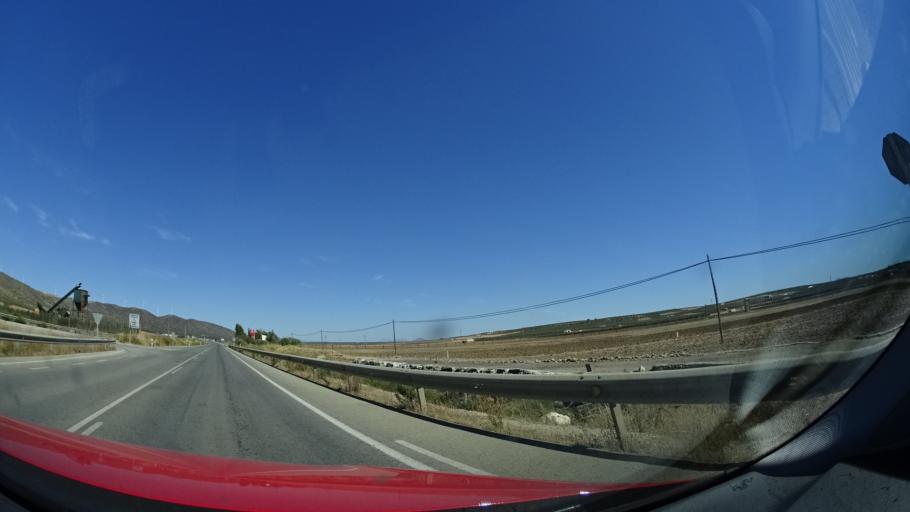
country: ES
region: Andalusia
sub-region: Provincia de Malaga
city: Sierra de Yeguas
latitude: 37.1336
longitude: -4.8614
